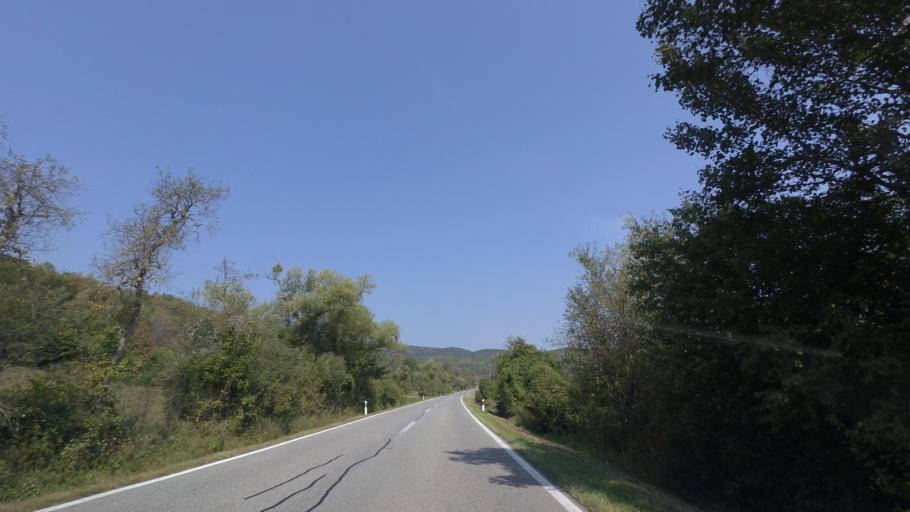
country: HR
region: Brodsko-Posavska
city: Resetari
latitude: 45.4051
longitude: 17.5009
